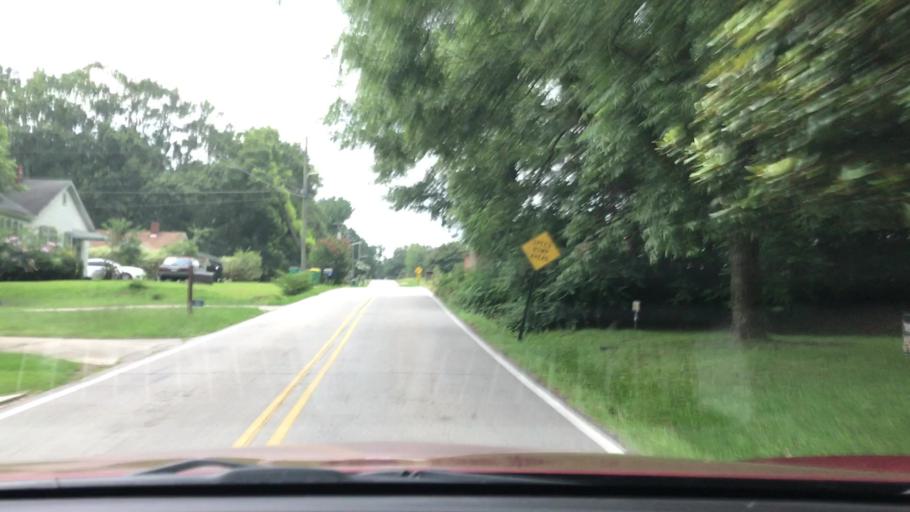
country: US
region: Georgia
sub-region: Barrow County
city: Winder
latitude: 33.9908
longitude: -83.7352
